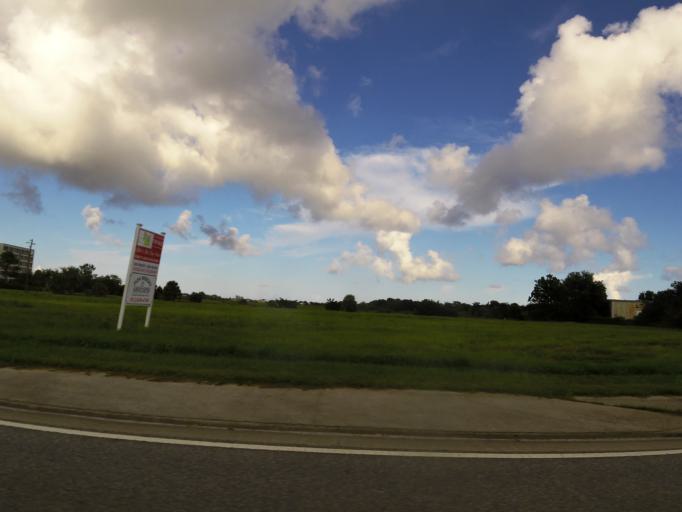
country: US
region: Georgia
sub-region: Glynn County
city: Brunswick
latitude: 31.1701
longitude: -81.4745
